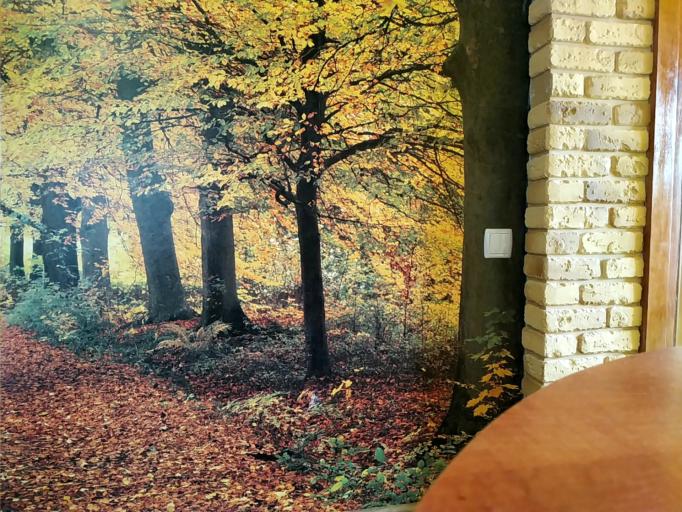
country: RU
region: Leningrad
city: Volosovo
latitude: 59.0299
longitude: 29.2904
